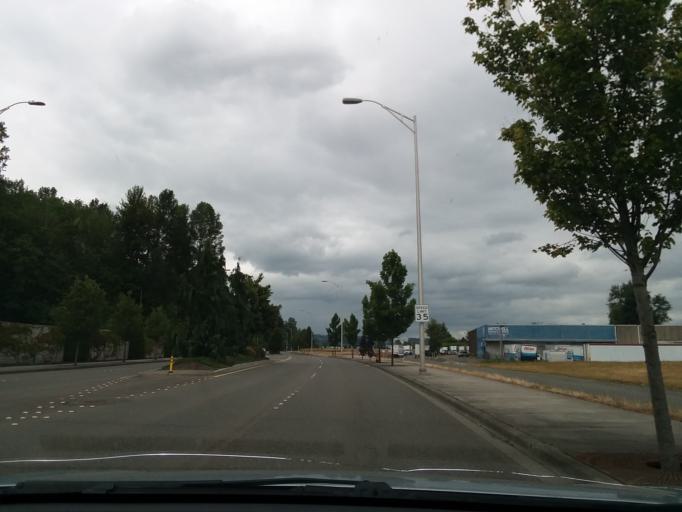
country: US
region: Washington
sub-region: King County
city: SeaTac
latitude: 47.4324
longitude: -122.2652
